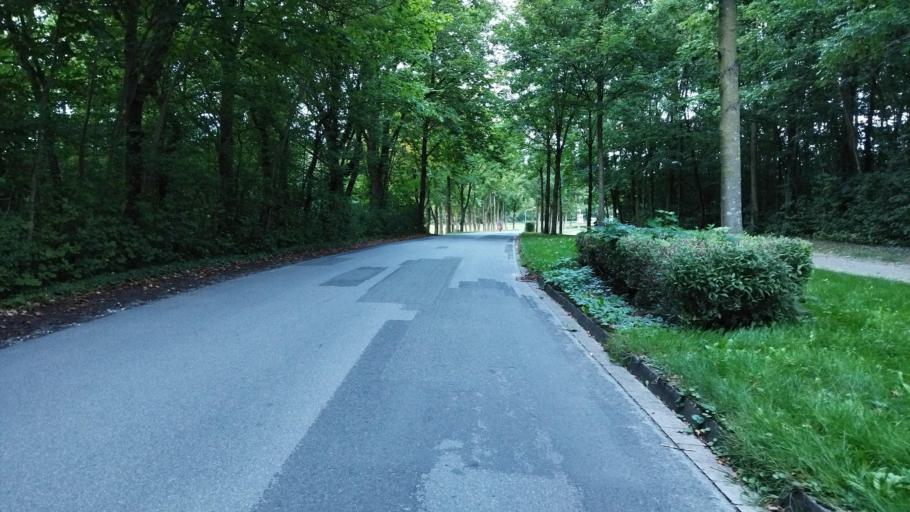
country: DE
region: Lower Saxony
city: Bad Laer
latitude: 52.1068
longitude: 8.0966
